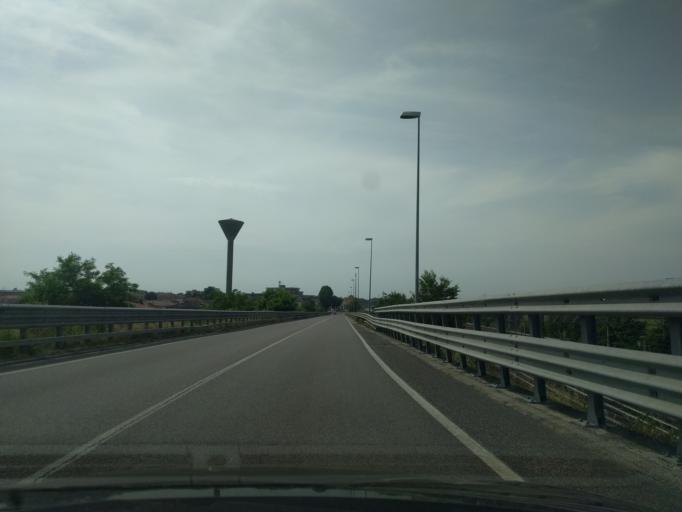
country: IT
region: Veneto
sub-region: Provincia di Verona
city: Nogara
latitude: 45.1773
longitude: 11.0743
